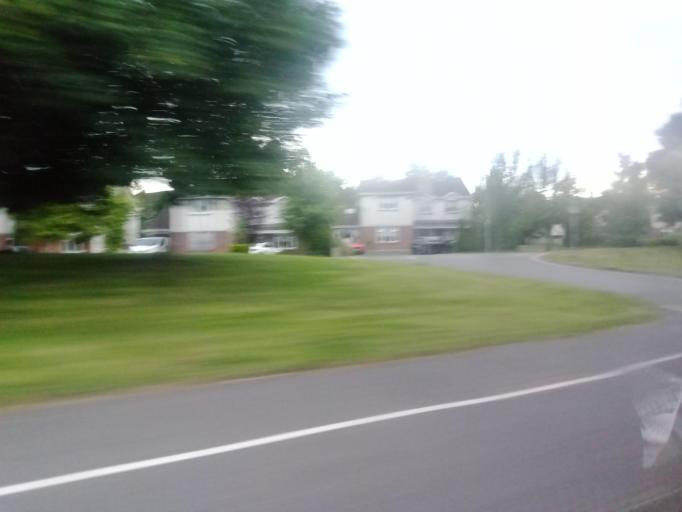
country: IE
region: Leinster
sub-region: Laois
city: Portlaoise
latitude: 53.0351
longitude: -7.3144
